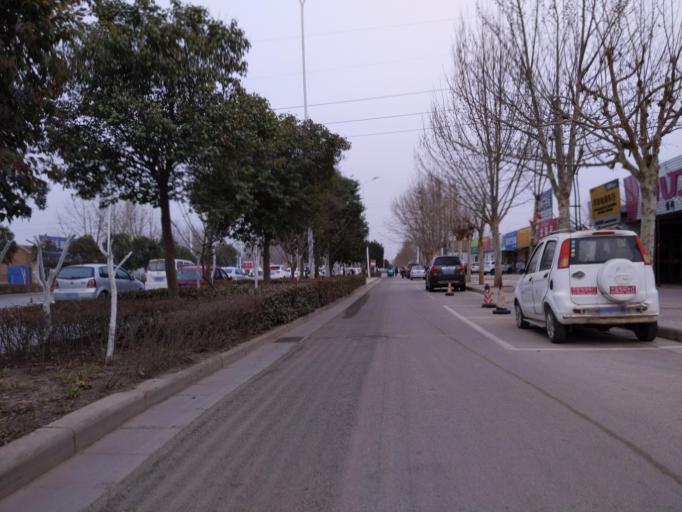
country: CN
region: Henan Sheng
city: Zhongyuanlu
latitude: 35.7546
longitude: 115.0942
